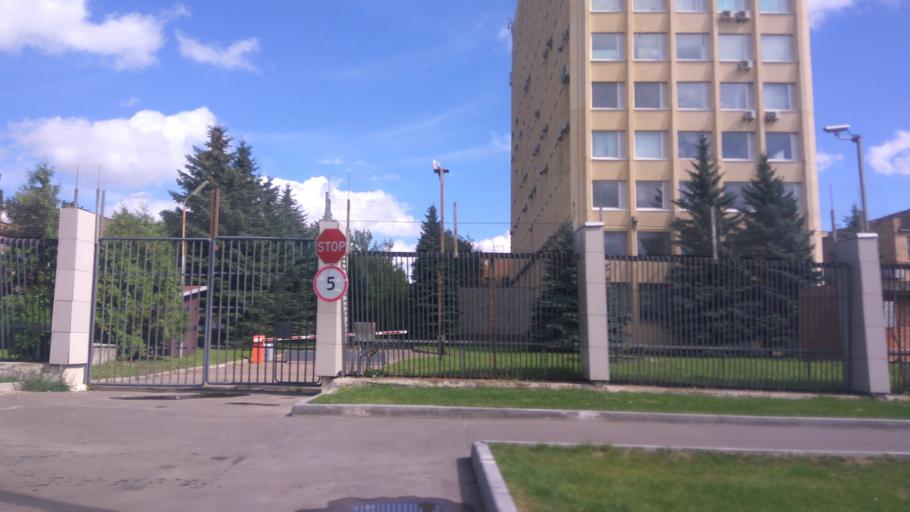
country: RU
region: Moscow
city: Kolomenskoye
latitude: 55.6479
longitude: 37.6665
